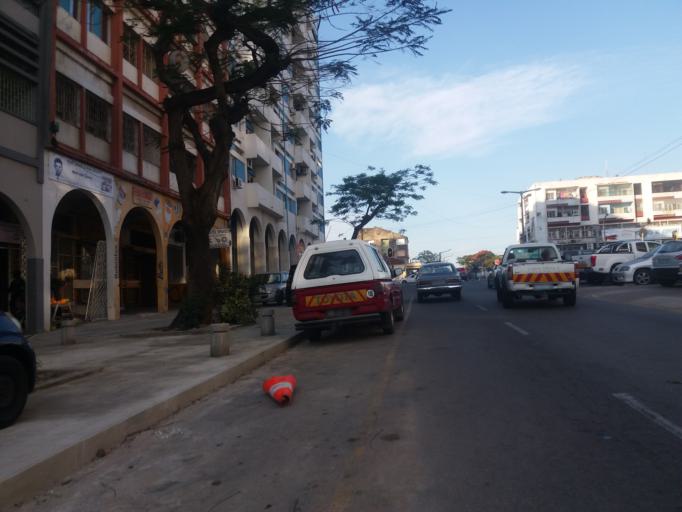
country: MZ
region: Maputo City
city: Maputo
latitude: -25.9615
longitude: 32.5698
